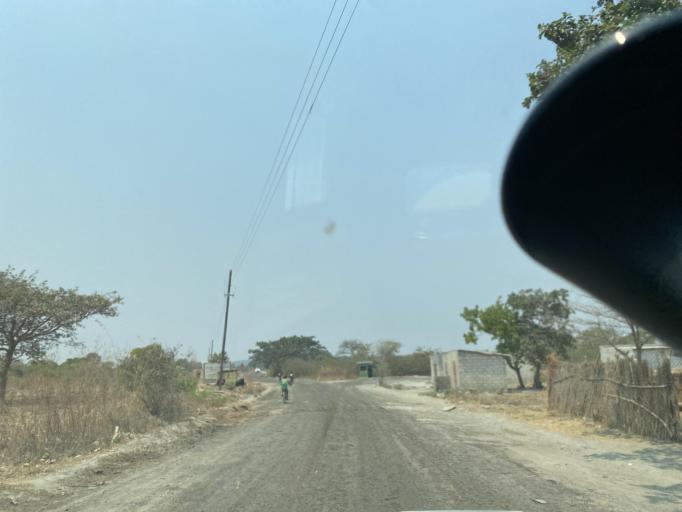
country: ZM
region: Lusaka
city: Lusaka
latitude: -15.5609
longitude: 28.4324
